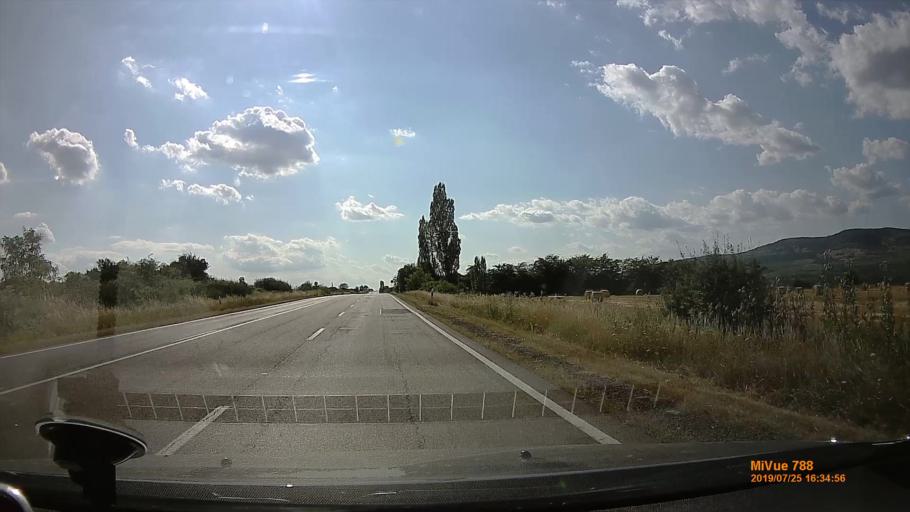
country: HU
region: Heves
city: Abasar
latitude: 47.7675
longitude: 20.0137
